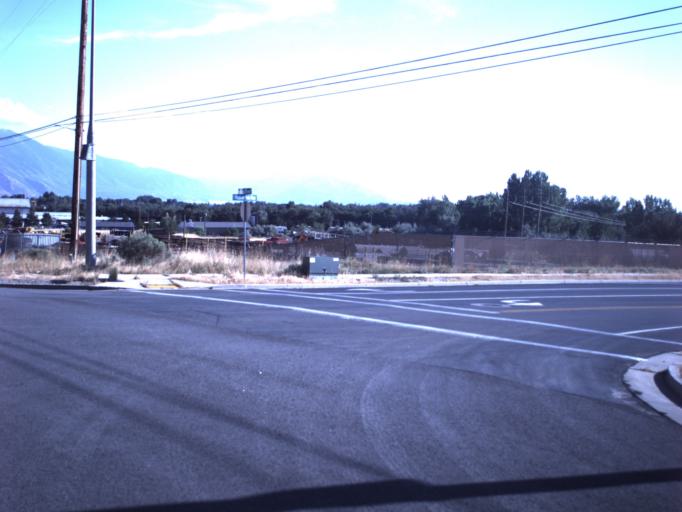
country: US
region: Utah
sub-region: Utah County
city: Springville
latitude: 40.1893
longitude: -111.6114
